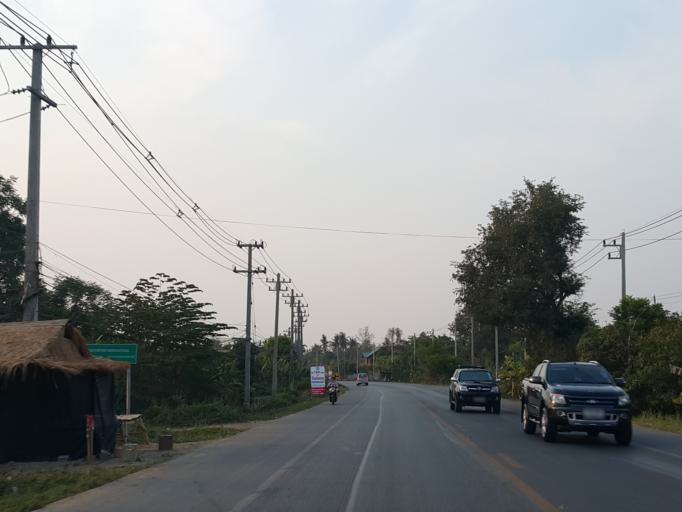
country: TH
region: Sukhothai
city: Sawankhalok
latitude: 17.2488
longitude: 99.8583
